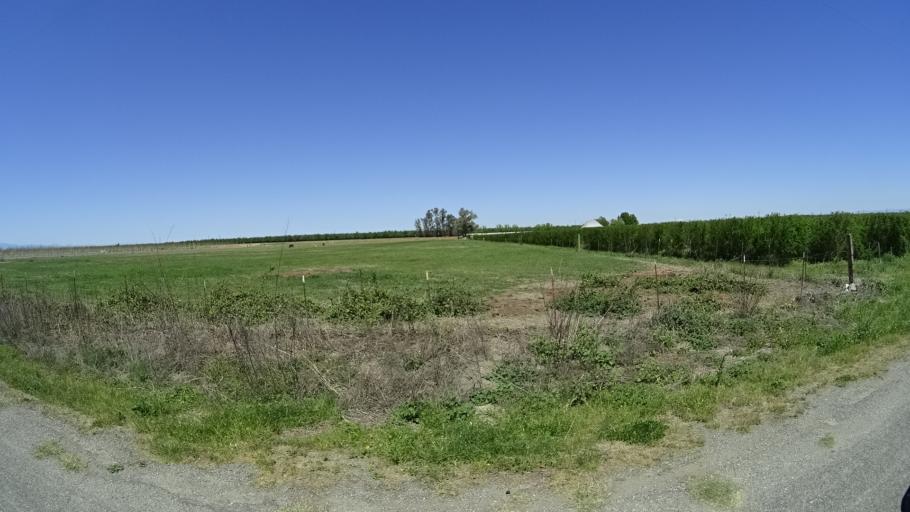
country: US
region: California
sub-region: Glenn County
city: Hamilton City
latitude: 39.7288
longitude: -122.0929
